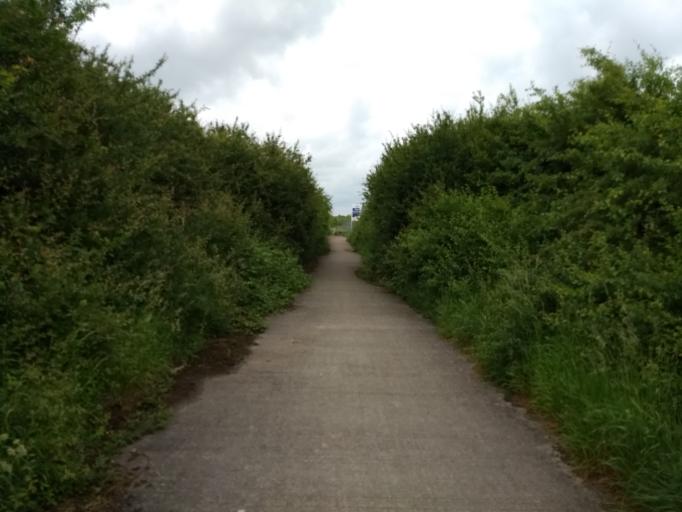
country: GB
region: England
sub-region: Central Bedfordshire
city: Marston Moretaine
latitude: 52.0643
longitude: -0.5601
